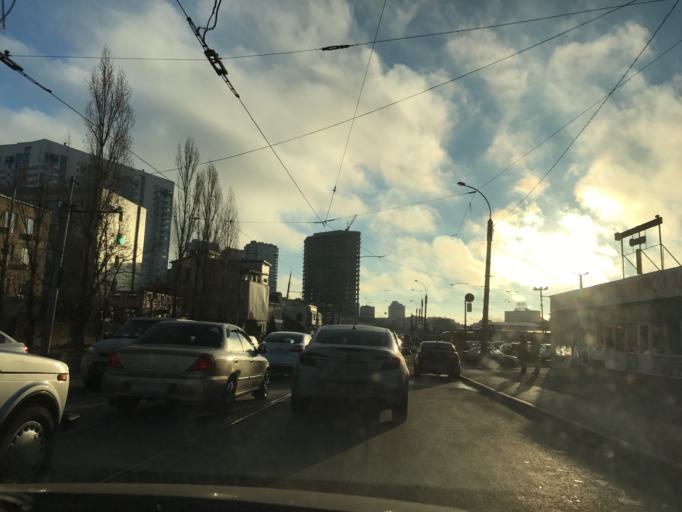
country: RU
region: Rostov
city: Rostov-na-Donu
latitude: 47.2241
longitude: 39.6870
